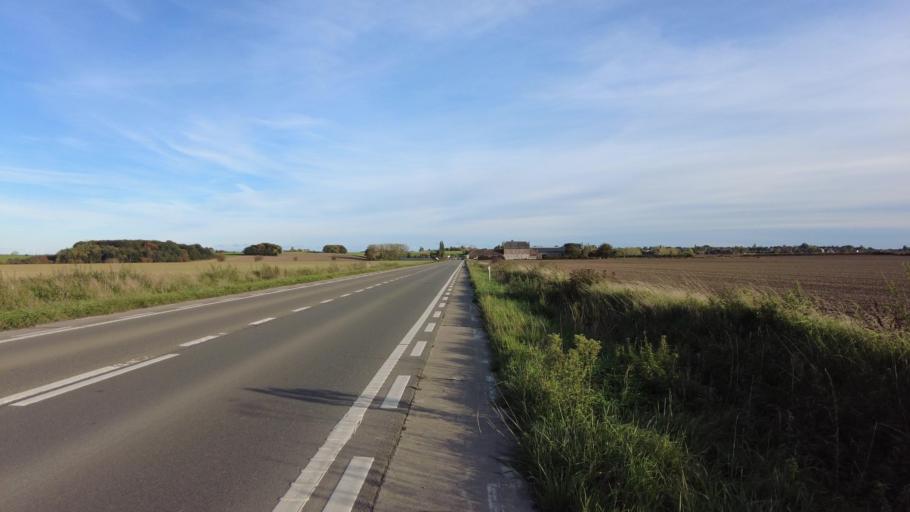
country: BE
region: Wallonia
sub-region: Province du Brabant Wallon
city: Jodoigne
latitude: 50.7080
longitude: 4.9097
